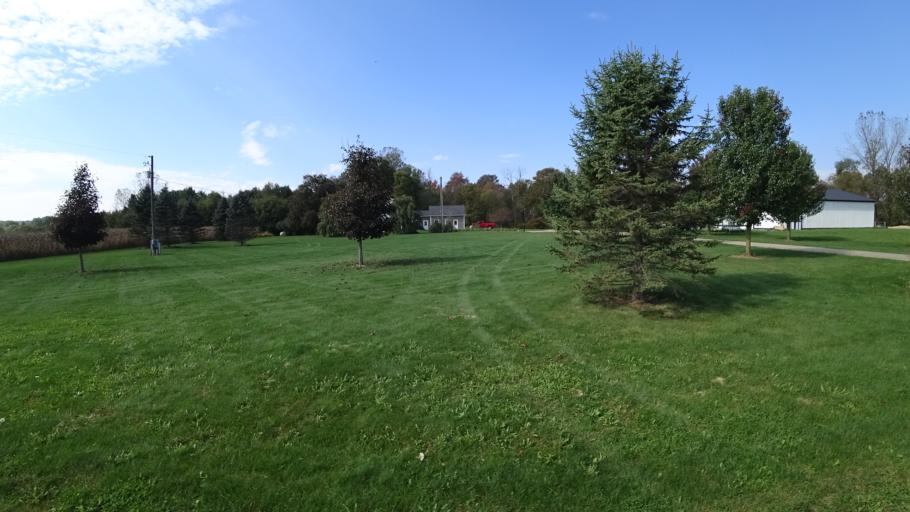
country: US
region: Michigan
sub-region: Saint Joseph County
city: Three Rivers
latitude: 41.9220
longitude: -85.6547
